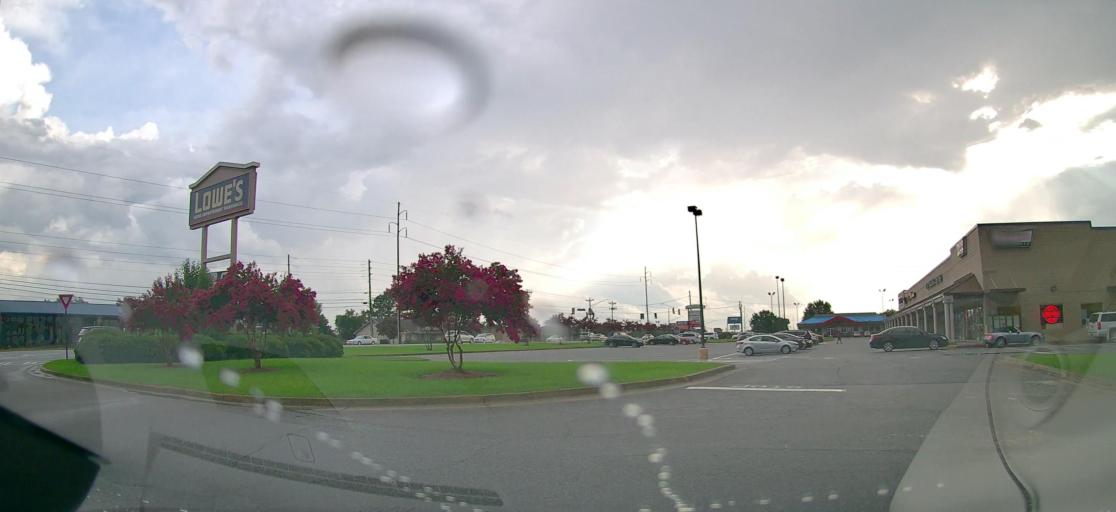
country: US
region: Georgia
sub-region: Houston County
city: Centerville
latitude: 32.6194
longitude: -83.6689
